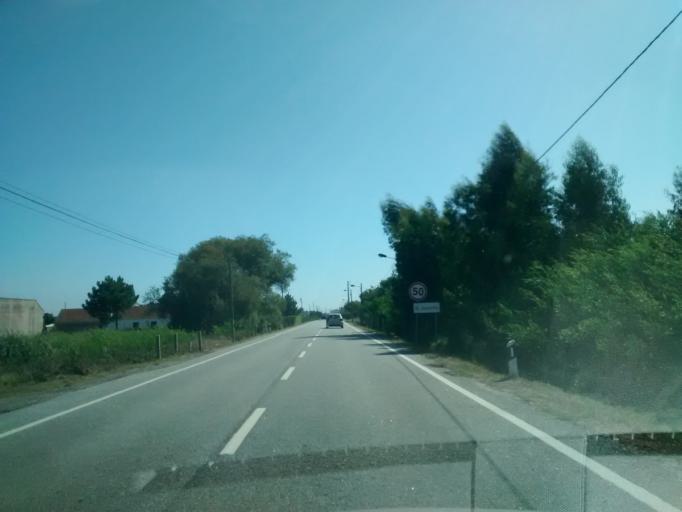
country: PT
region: Aveiro
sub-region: Ilhavo
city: Gafanha da Nazare
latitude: 40.6685
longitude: -8.7265
